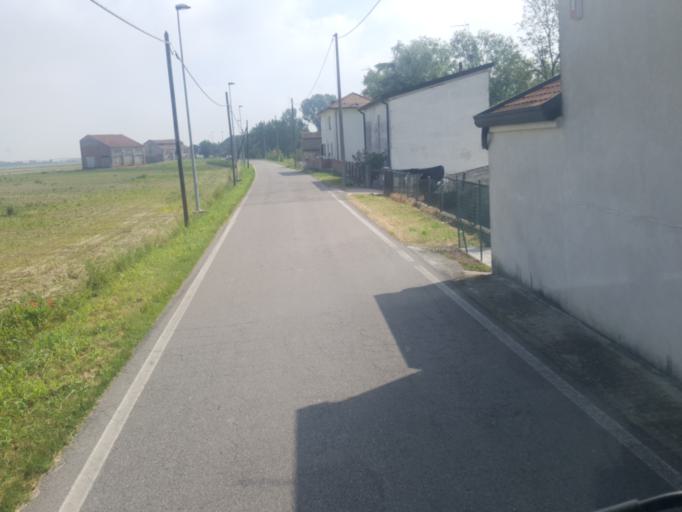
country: IT
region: Veneto
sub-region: Provincia di Rovigo
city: Canaro
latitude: 44.9351
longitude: 11.6656
